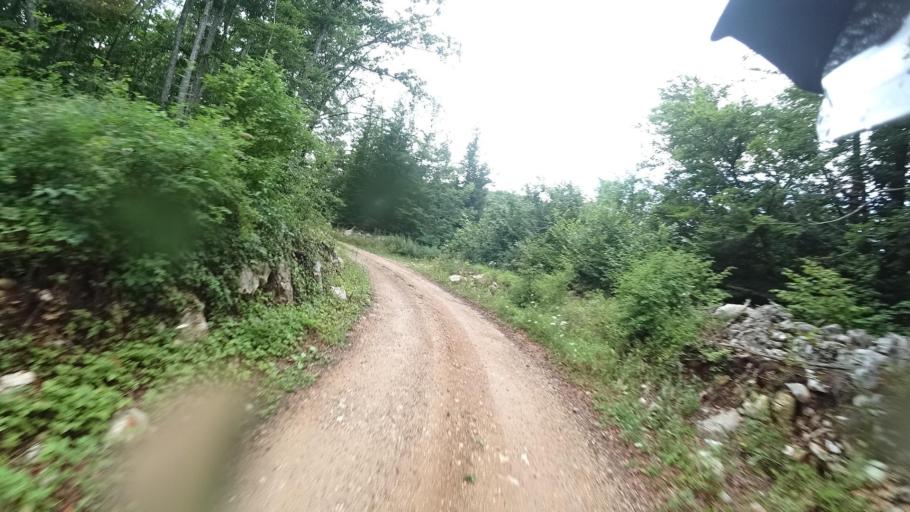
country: HR
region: Licko-Senjska
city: Jezerce
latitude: 44.7263
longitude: 15.6492
